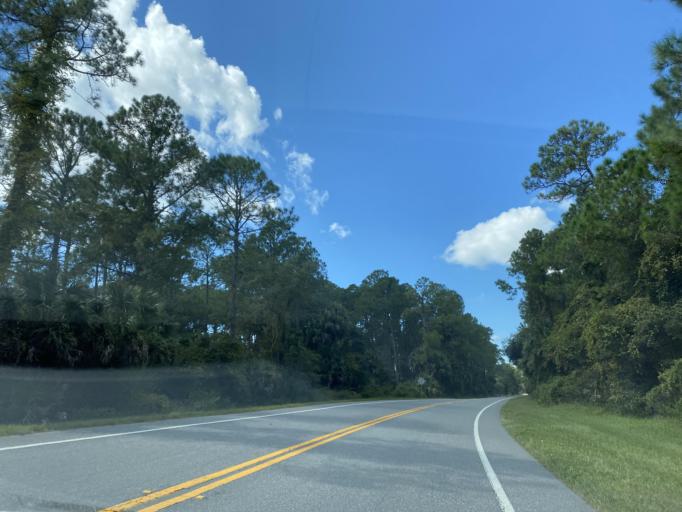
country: US
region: Florida
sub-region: Lake County
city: Lake Mack-Forest Hills
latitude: 29.0058
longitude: -81.4488
